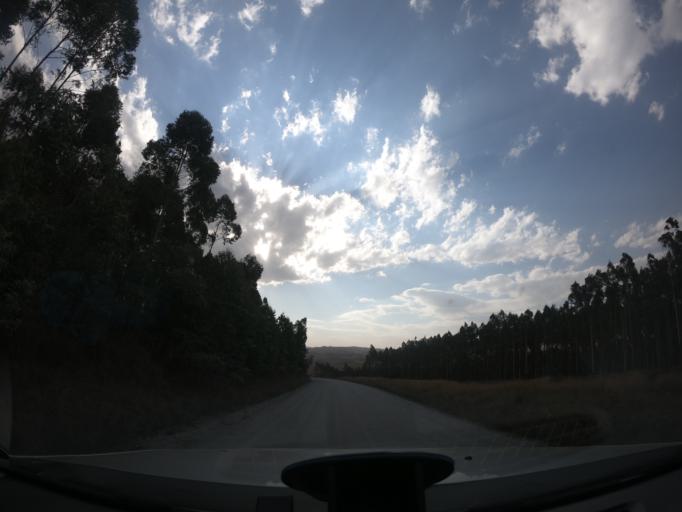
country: ZA
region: KwaZulu-Natal
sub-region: uMgungundlovu District Municipality
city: Howick
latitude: -29.4226
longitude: 30.1043
